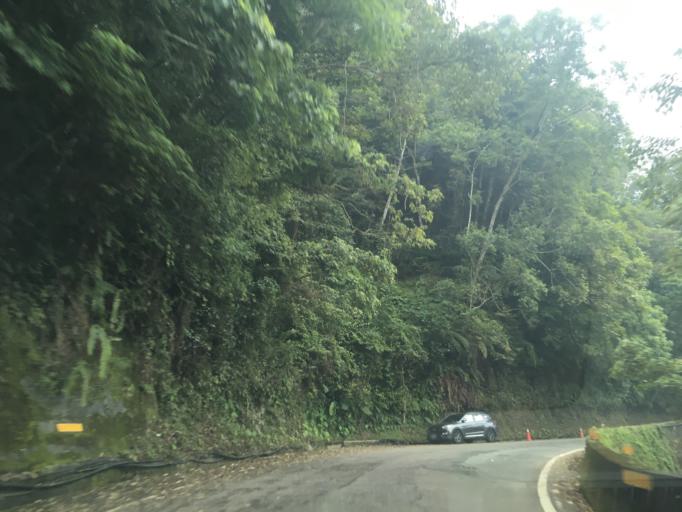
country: TW
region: Taiwan
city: Fengyuan
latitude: 24.2478
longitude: 120.9186
